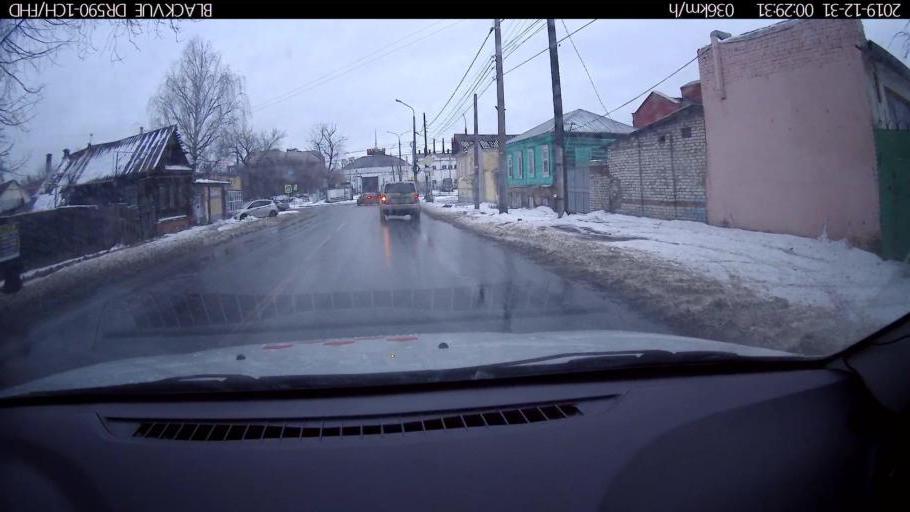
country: RU
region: Nizjnij Novgorod
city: Nizhniy Novgorod
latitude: 56.3158
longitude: 43.9526
